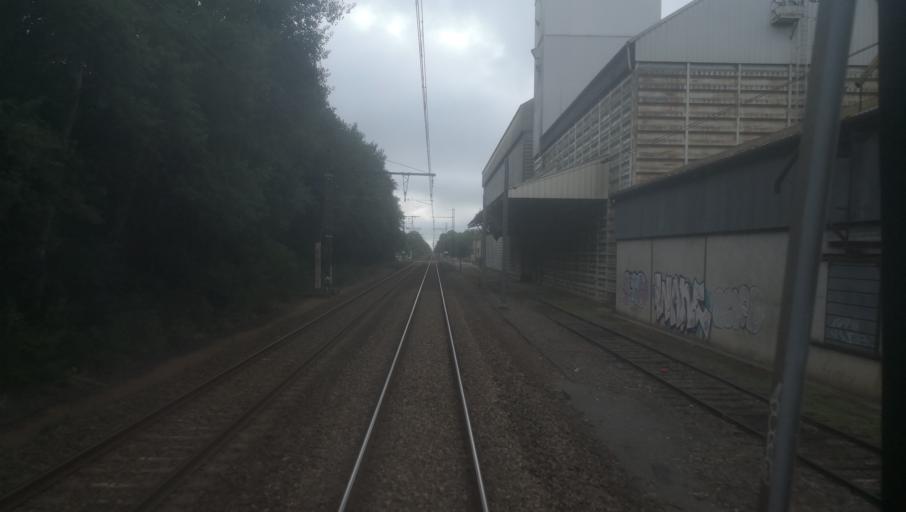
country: FR
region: Centre
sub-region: Departement de l'Indre
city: Montierchaume
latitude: 46.8496
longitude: 1.7916
